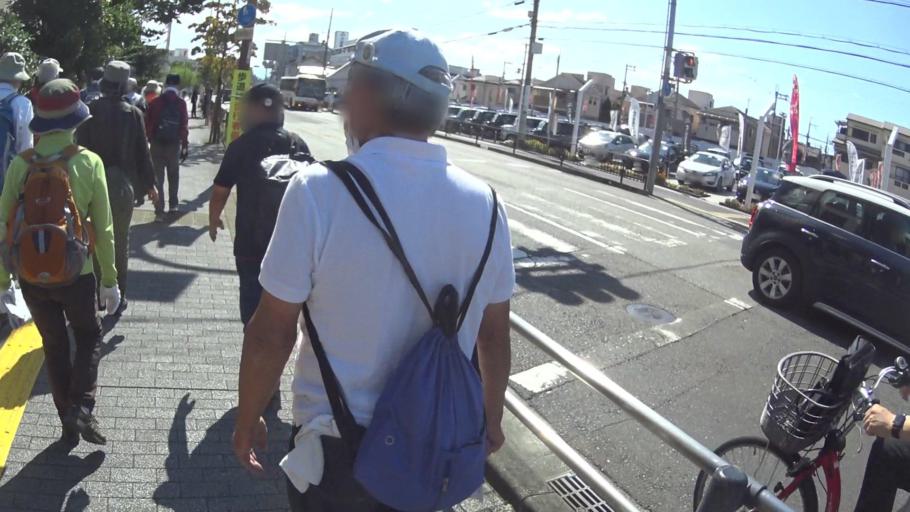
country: JP
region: Ehime
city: Kihoku-cho
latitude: 33.3918
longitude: 132.8469
